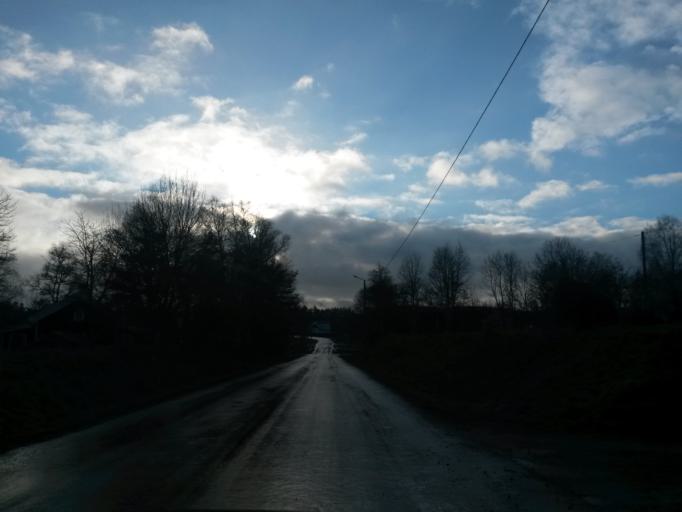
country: SE
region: Vaestra Goetaland
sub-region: Boras Kommun
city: Boras
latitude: 57.8607
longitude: 12.9288
